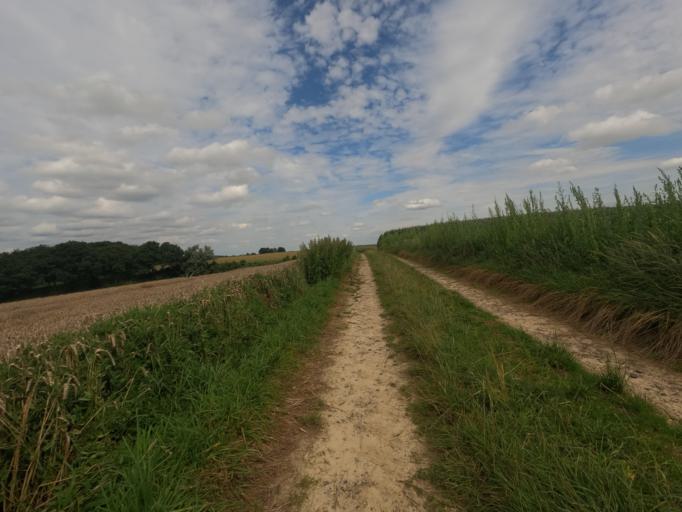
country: DE
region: North Rhine-Westphalia
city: Geilenkirchen
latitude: 50.9792
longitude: 6.1591
